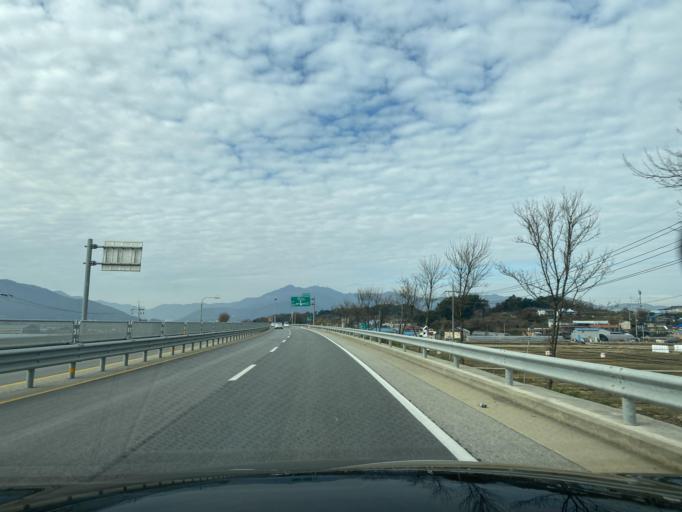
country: KR
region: Chungcheongnam-do
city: Hongsung
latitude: 36.6909
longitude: 126.7007
